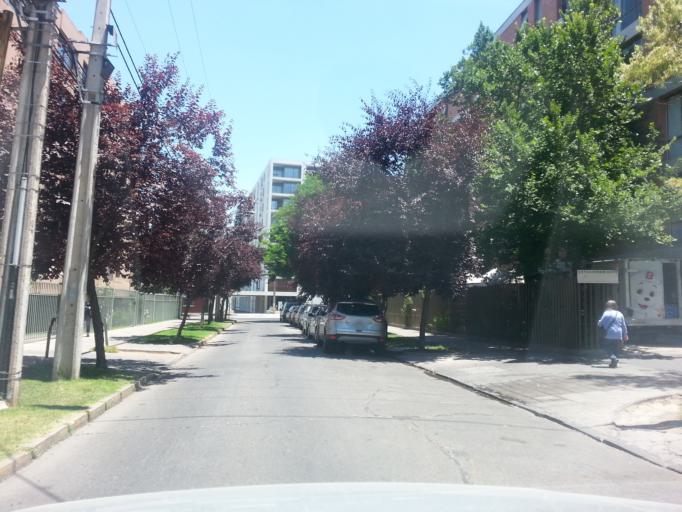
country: CL
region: Santiago Metropolitan
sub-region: Provincia de Santiago
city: Santiago
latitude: -33.4352
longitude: -70.6144
